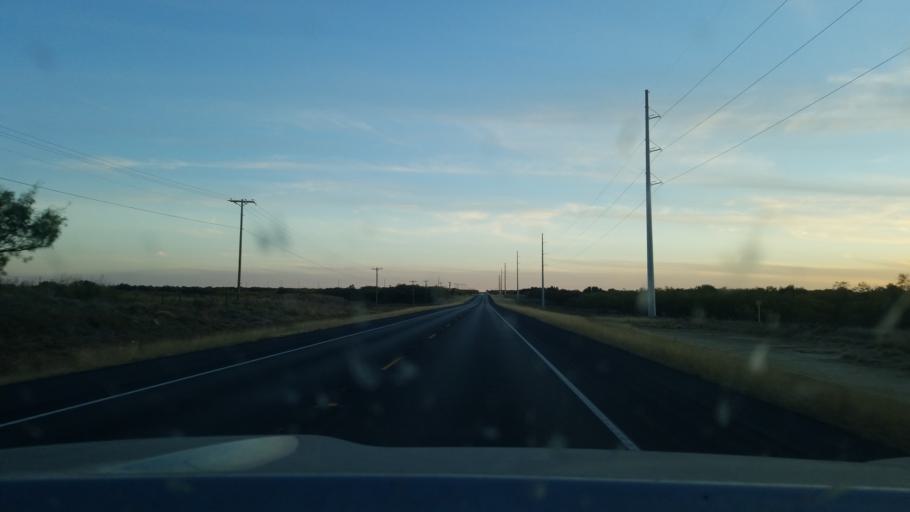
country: US
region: Texas
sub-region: Stephens County
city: Breckenridge
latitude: 32.7061
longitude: -98.9029
